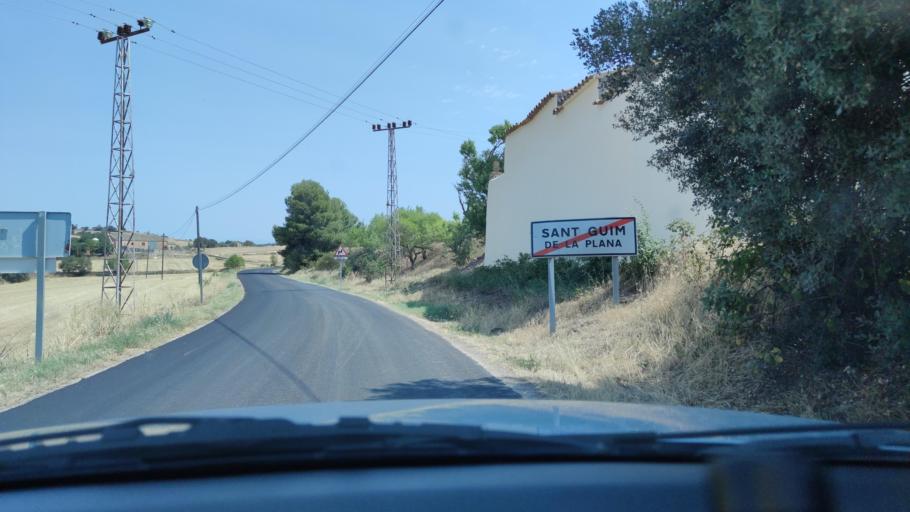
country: ES
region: Catalonia
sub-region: Provincia de Lleida
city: Ivorra
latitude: 41.7638
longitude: 1.3249
